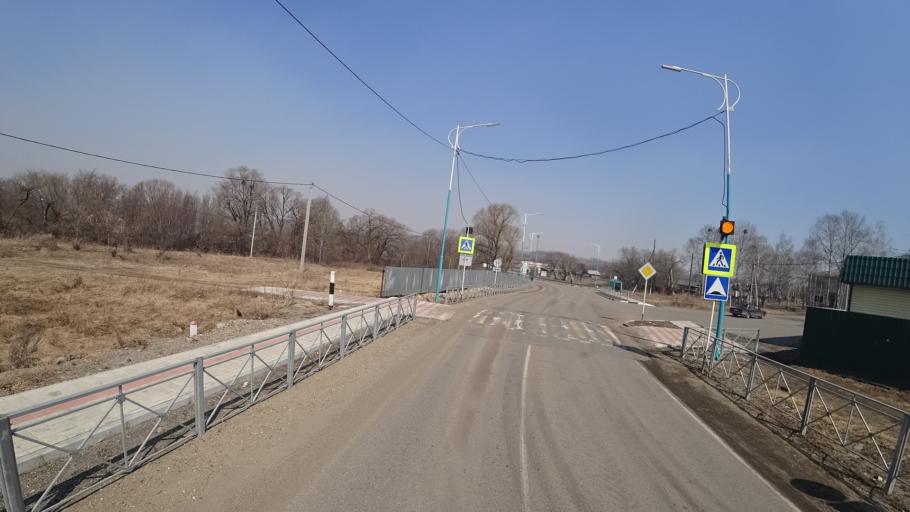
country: RU
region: Amur
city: Novobureyskiy
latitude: 49.7926
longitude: 129.9052
